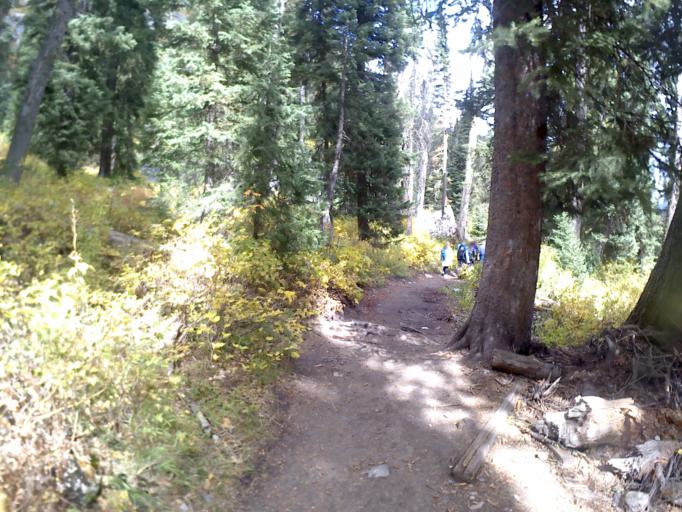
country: US
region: Wyoming
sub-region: Teton County
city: Moose Wilson Road
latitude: 43.7687
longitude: -110.7504
